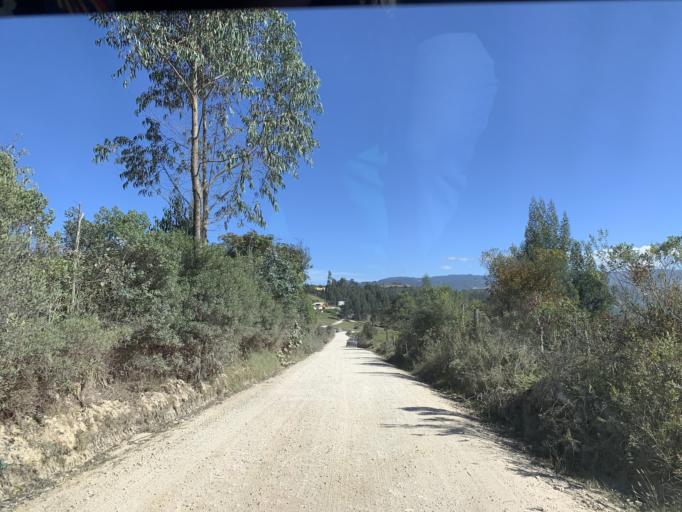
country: CO
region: Boyaca
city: Tuta
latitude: 5.7080
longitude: -73.1531
